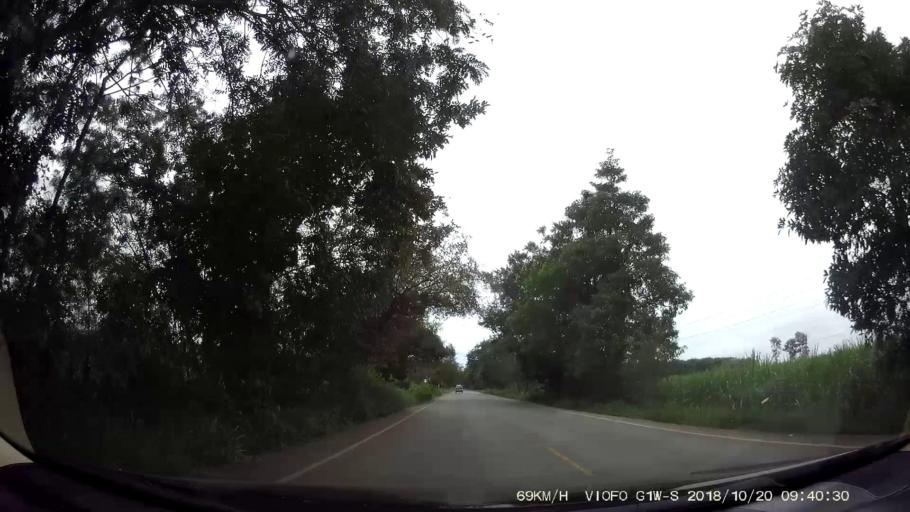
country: TH
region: Chaiyaphum
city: Kaset Sombun
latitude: 16.4437
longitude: 101.9612
